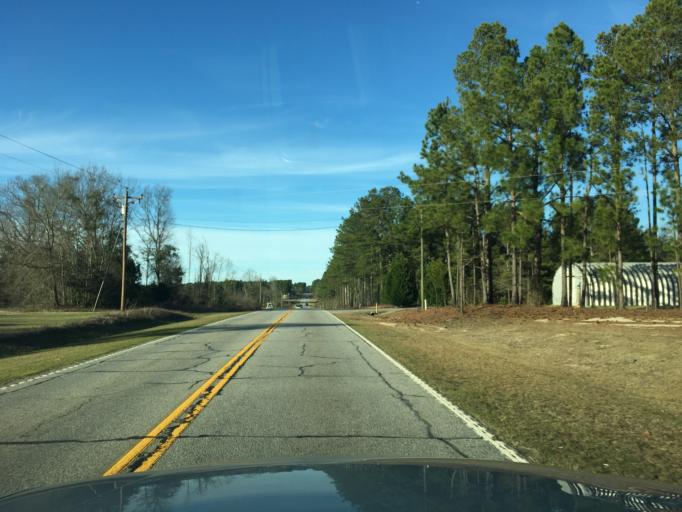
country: US
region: South Carolina
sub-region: Edgefield County
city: Johnston
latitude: 33.7525
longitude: -81.6433
